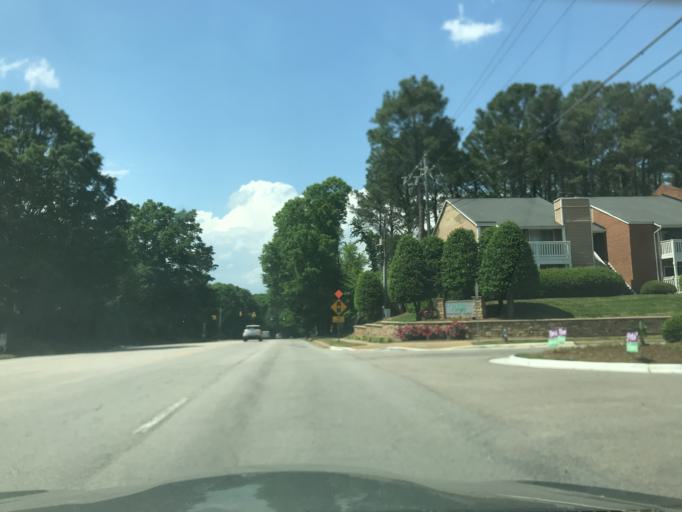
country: US
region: North Carolina
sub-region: Wake County
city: West Raleigh
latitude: 35.8725
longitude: -78.6424
